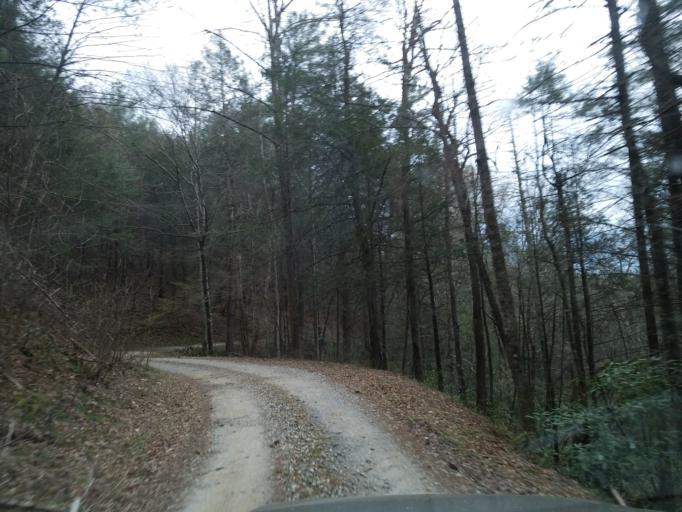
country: US
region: Georgia
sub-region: Union County
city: Blairsville
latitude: 34.7774
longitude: -84.0976
